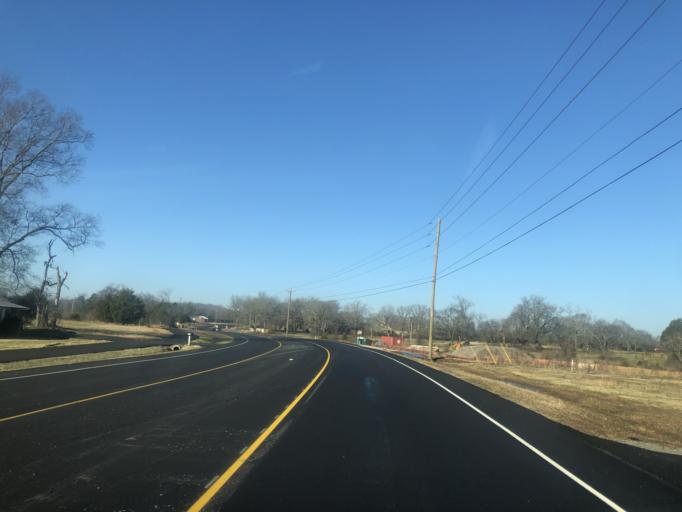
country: US
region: Tennessee
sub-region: Williamson County
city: Nolensville
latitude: 35.9608
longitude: -86.6800
